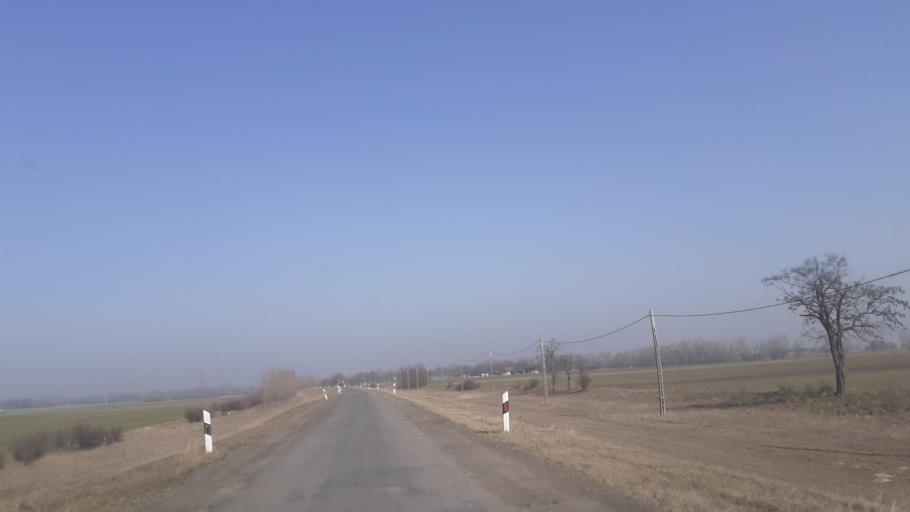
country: HU
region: Pest
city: Domsod
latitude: 47.0614
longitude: 18.9984
